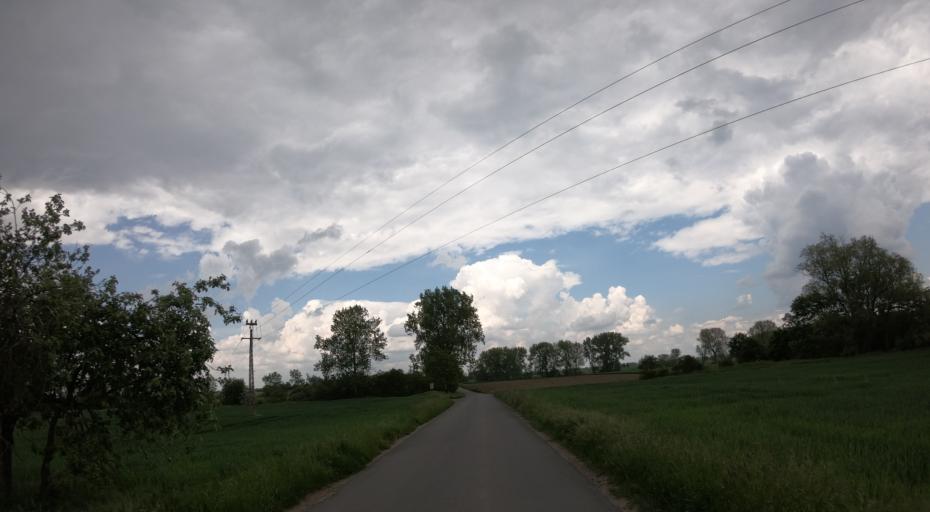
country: PL
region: West Pomeranian Voivodeship
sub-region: Powiat pyrzycki
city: Bielice
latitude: 53.2229
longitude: 14.7671
